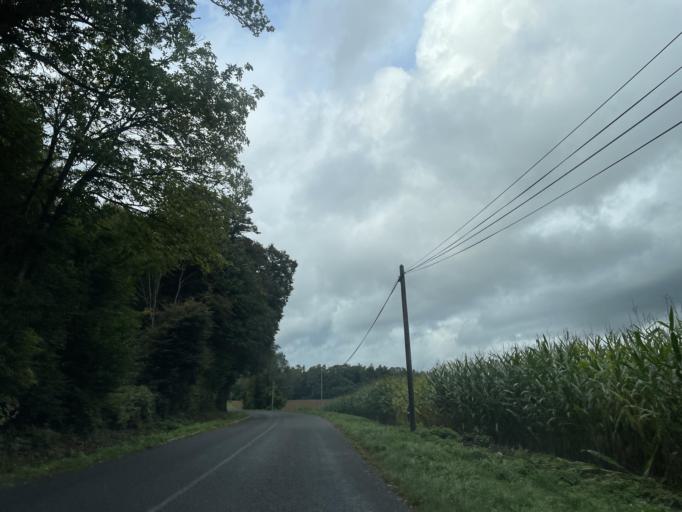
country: FR
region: Ile-de-France
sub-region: Departement de Seine-et-Marne
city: Saint-Jean-les-Deux-Jumeaux
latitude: 48.9099
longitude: 3.0212
